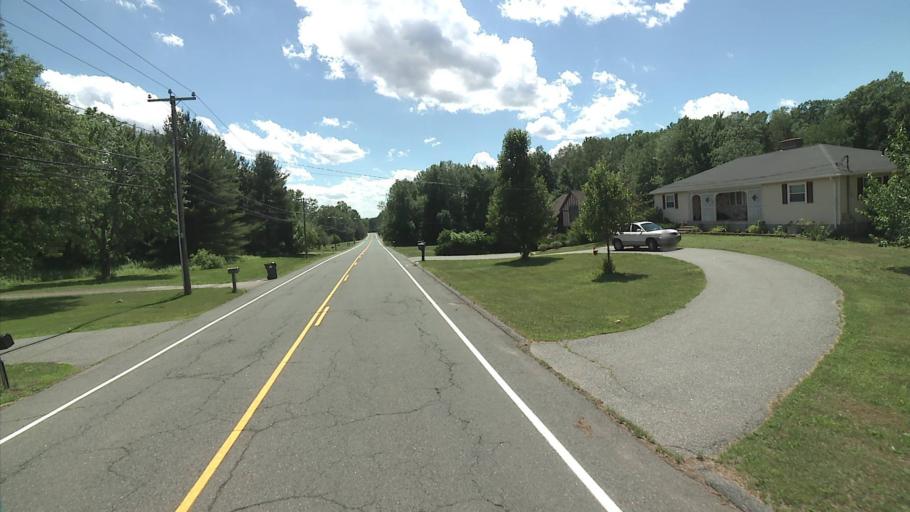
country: US
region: Connecticut
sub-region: Tolland County
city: Somers
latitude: 42.0080
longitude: -72.4849
